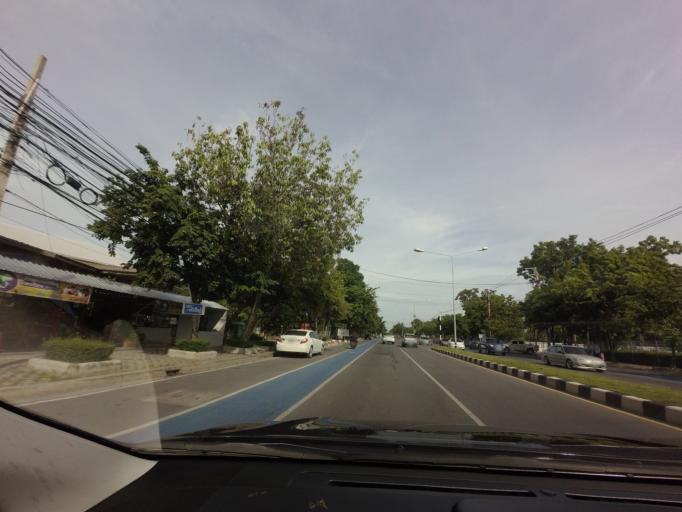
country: TH
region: Chon Buri
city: Chon Buri
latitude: 13.2960
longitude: 100.9087
